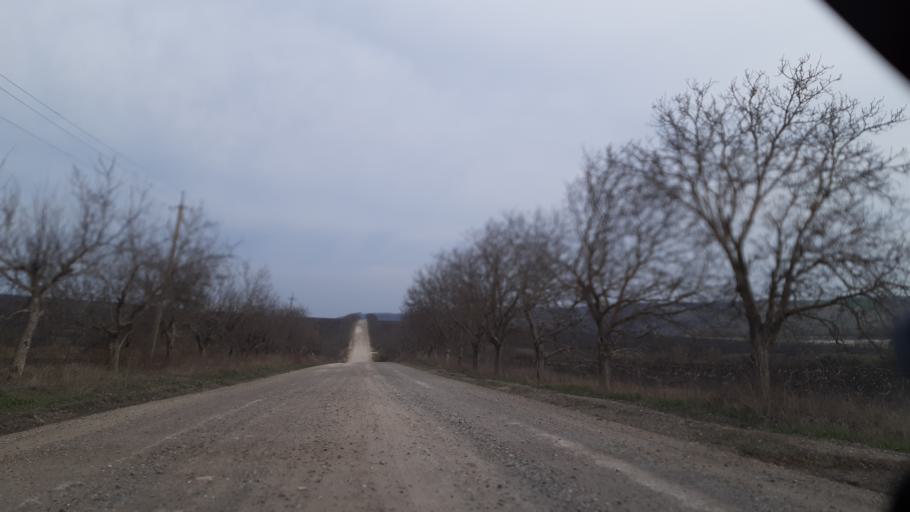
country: MD
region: Soldanesti
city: Soldanesti
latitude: 47.6988
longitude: 28.7260
